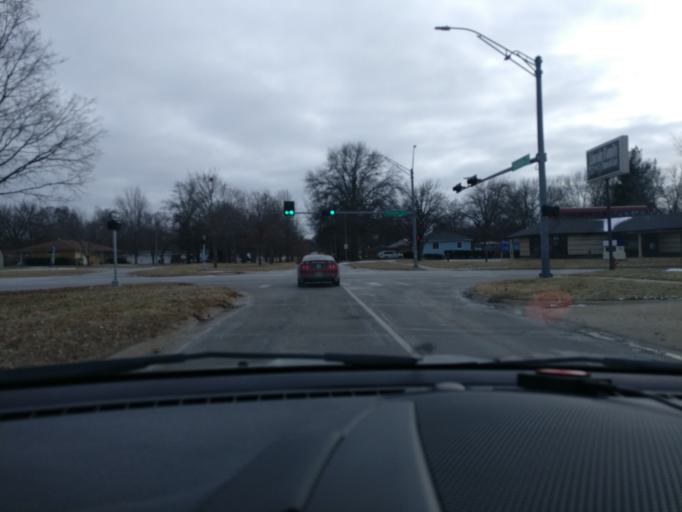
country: US
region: Nebraska
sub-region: Lancaster County
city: Lincoln
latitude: 40.8490
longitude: -96.6402
